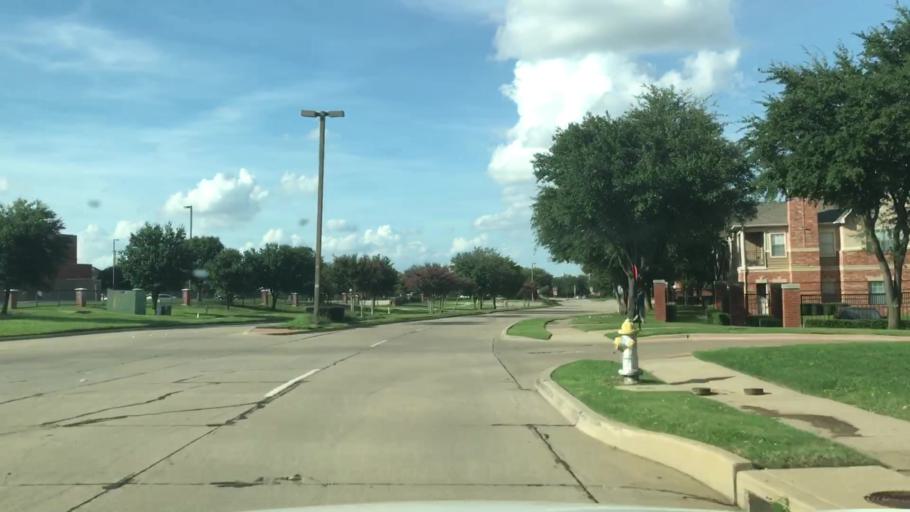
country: US
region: Texas
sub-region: Dallas County
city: Farmers Branch
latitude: 32.9256
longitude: -96.9578
